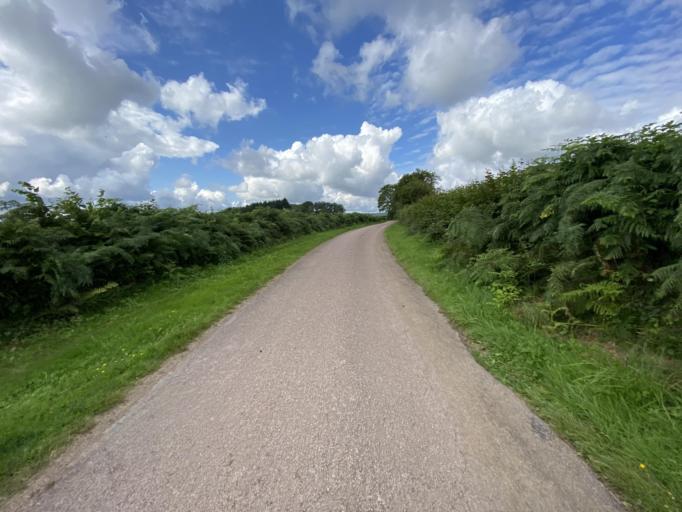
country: FR
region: Bourgogne
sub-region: Departement de la Cote-d'Or
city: Saulieu
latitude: 47.2748
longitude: 4.1934
